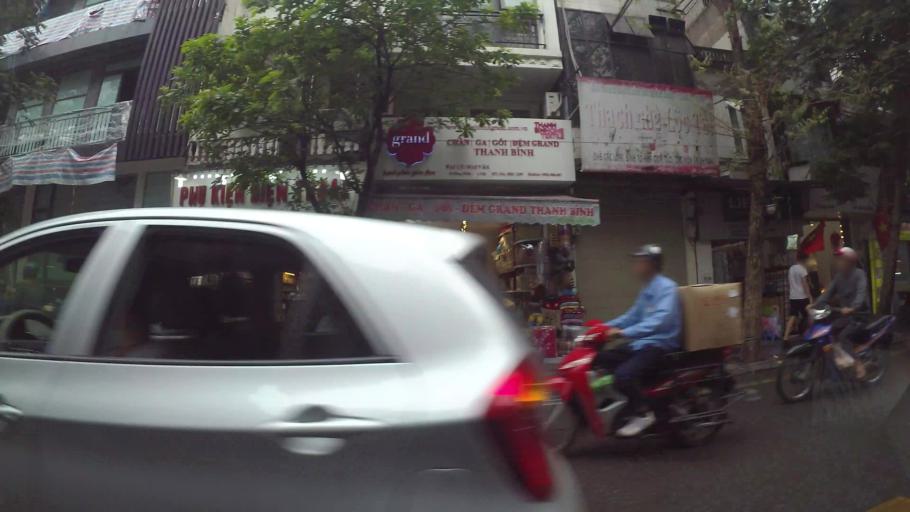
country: VN
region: Ha Noi
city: Hoan Kiem
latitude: 21.0323
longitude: 105.8468
